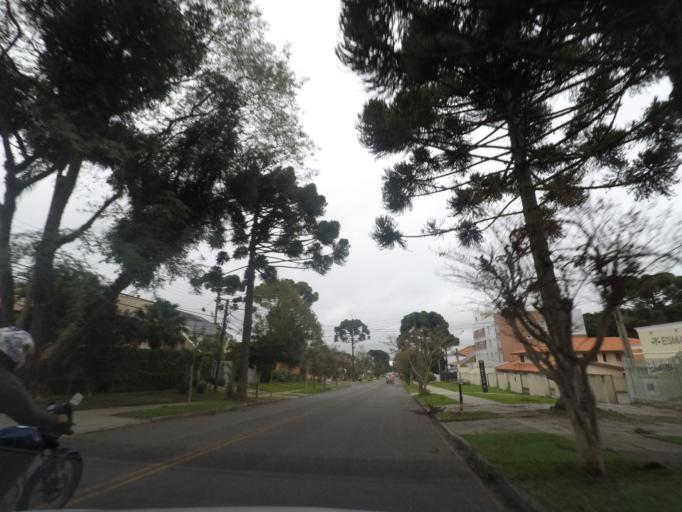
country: BR
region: Parana
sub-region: Curitiba
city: Curitiba
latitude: -25.4016
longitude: -49.2647
